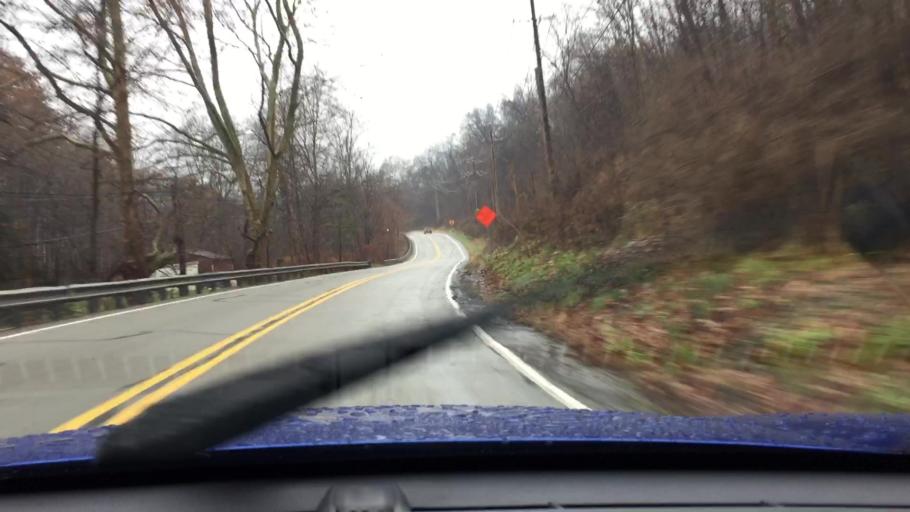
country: US
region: Pennsylvania
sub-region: Washington County
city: Canonsburg
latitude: 40.2859
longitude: -80.1553
